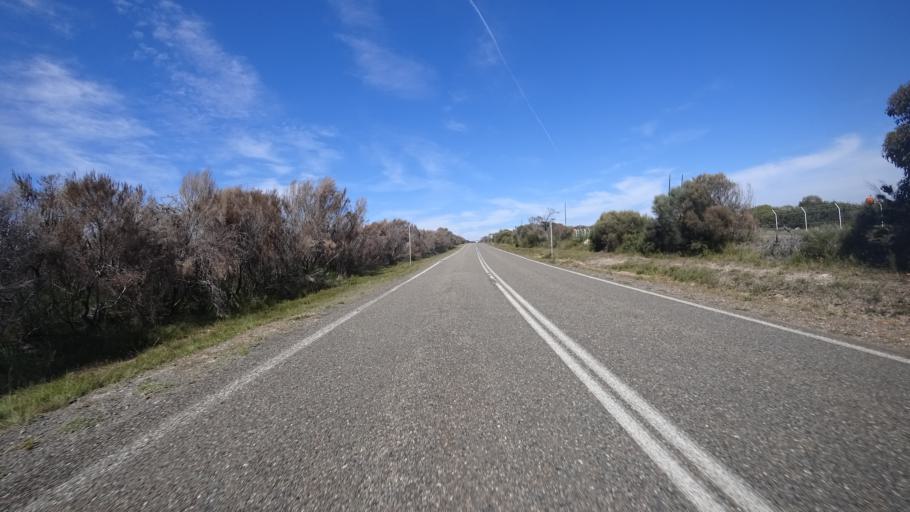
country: AU
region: New South Wales
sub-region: Shoalhaven Shire
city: Falls Creek
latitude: -35.1461
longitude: 150.7080
